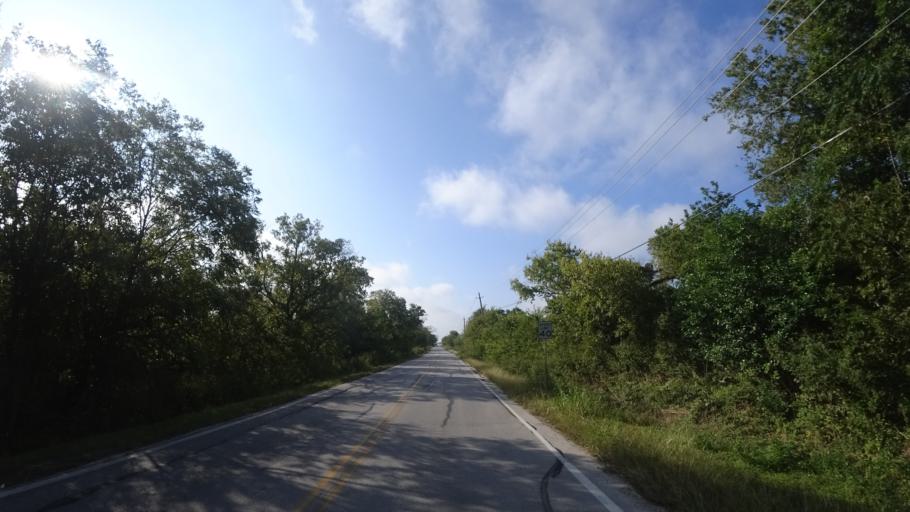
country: US
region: Texas
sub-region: Travis County
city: Manor
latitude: 30.3515
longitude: -97.6465
